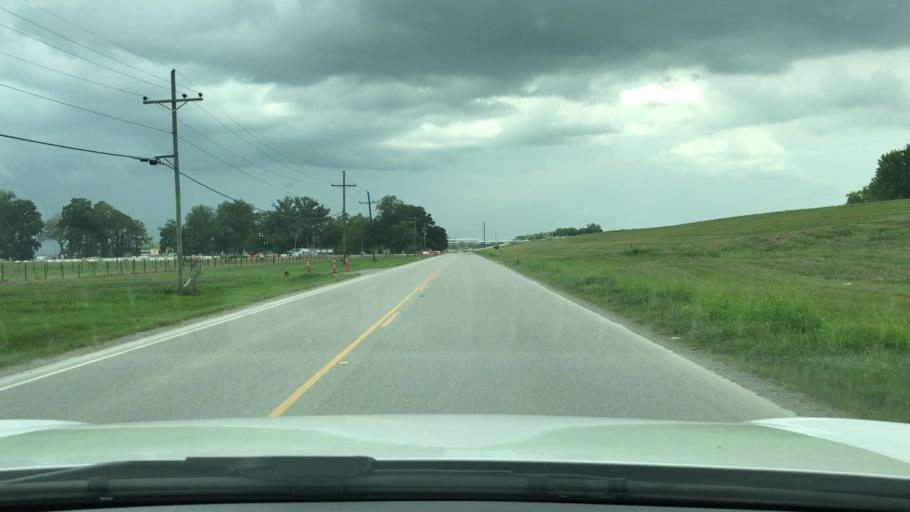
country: US
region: Louisiana
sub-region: Iberville Parish
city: Plaquemine
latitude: 30.2735
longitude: -91.1750
